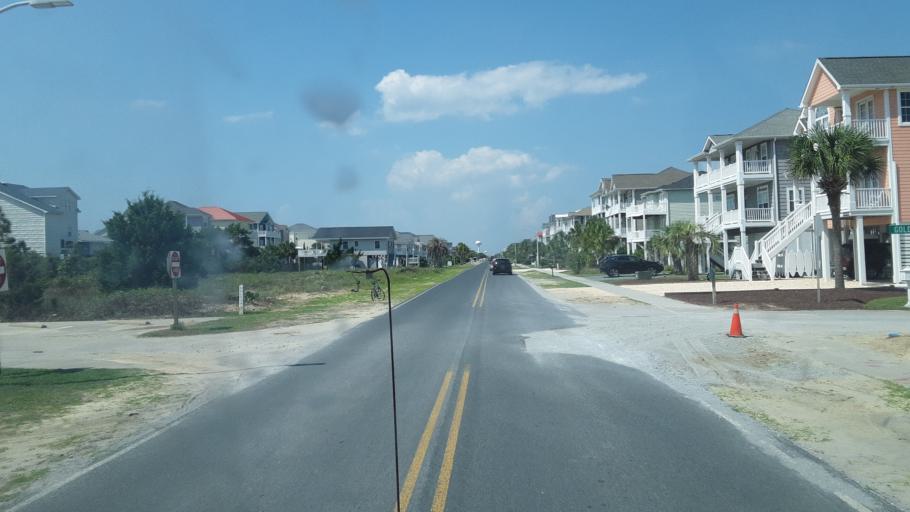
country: US
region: North Carolina
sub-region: Brunswick County
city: Shallotte
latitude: 33.8937
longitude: -78.4156
